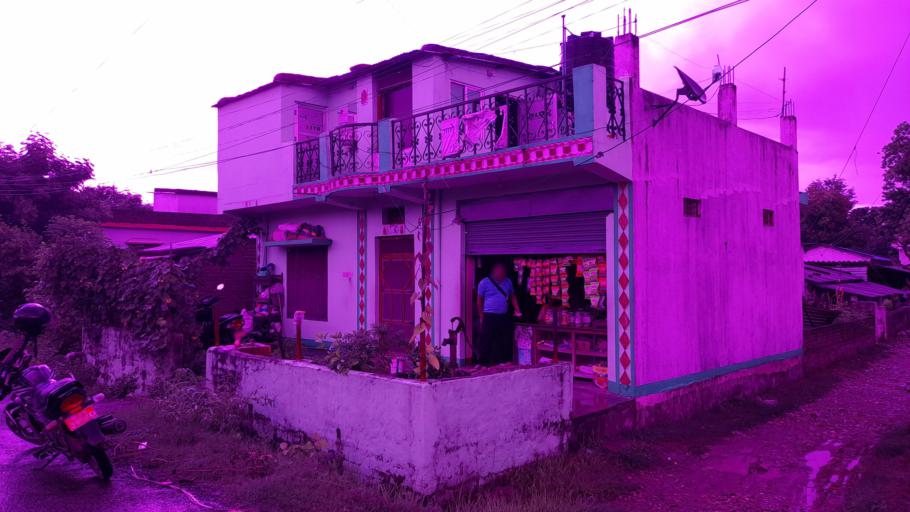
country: NP
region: Mid Western
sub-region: Bheri Zone
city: Nepalgunj
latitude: 28.1941
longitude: 81.6974
